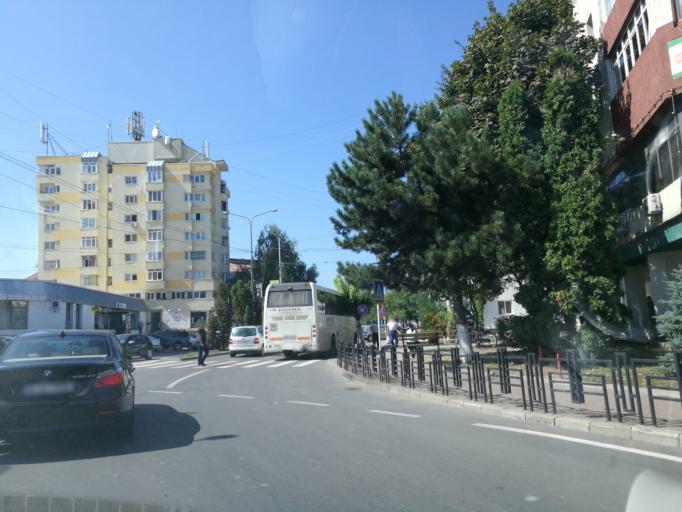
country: RO
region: Suceava
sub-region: Municipiul Suceava
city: Radauti
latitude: 47.8469
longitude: 25.9139
